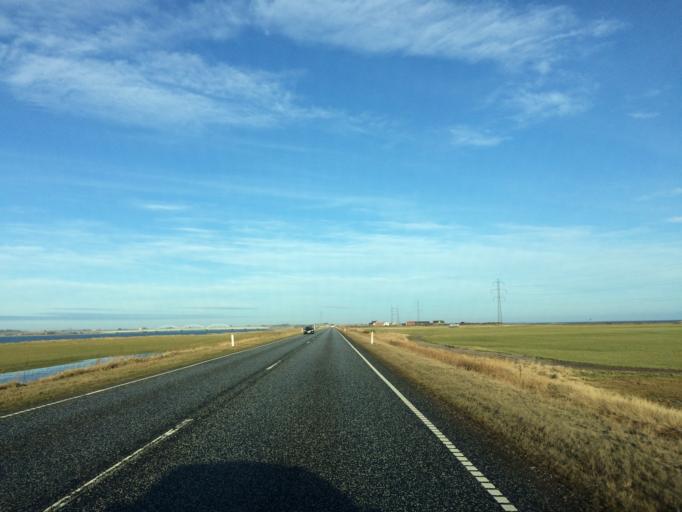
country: DK
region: Central Jutland
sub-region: Struer Kommune
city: Struer
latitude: 56.5634
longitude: 8.5583
